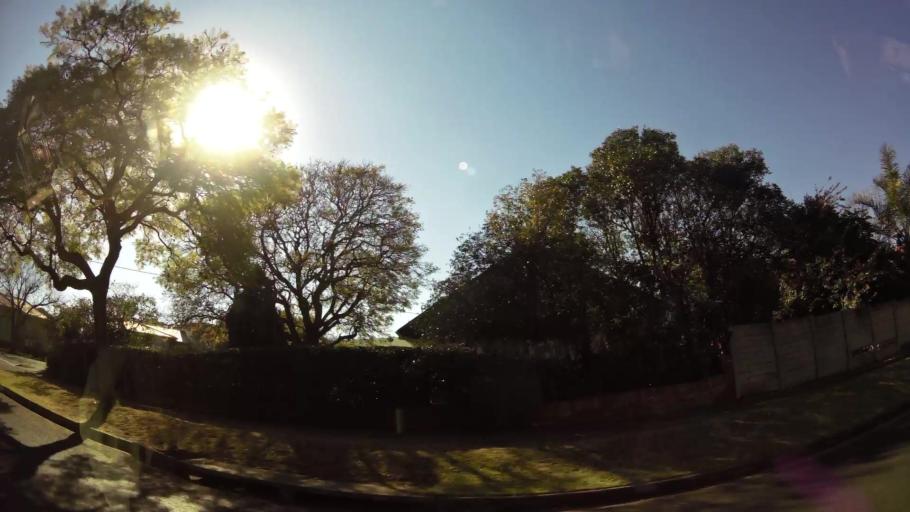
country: ZA
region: Gauteng
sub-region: City of Johannesburg Metropolitan Municipality
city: Johannesburg
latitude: -26.1927
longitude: 27.9837
